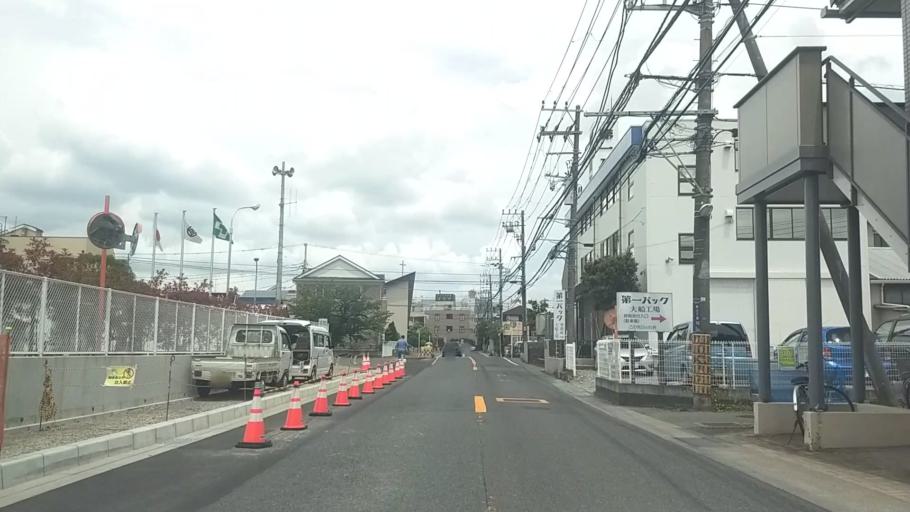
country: JP
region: Kanagawa
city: Kamakura
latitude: 35.3475
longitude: 139.5279
